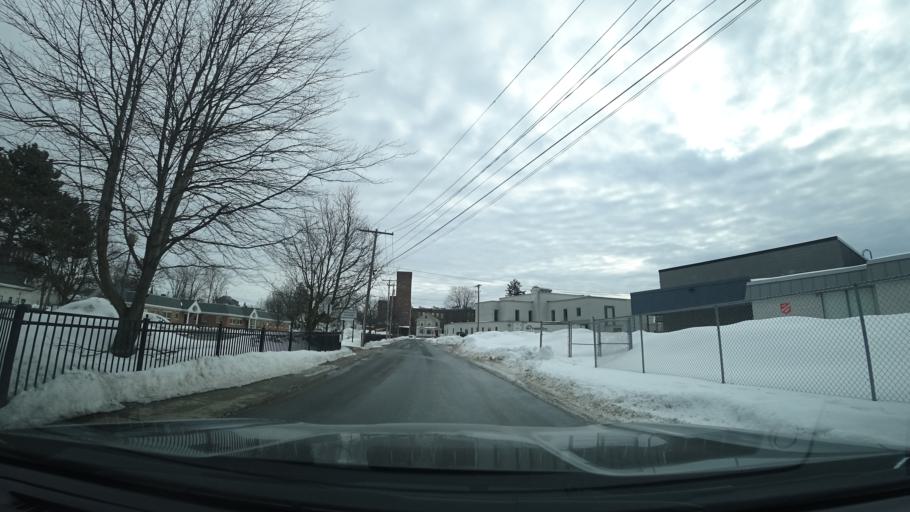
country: US
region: New York
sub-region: Warren County
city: Glens Falls
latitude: 43.3087
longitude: -73.6509
